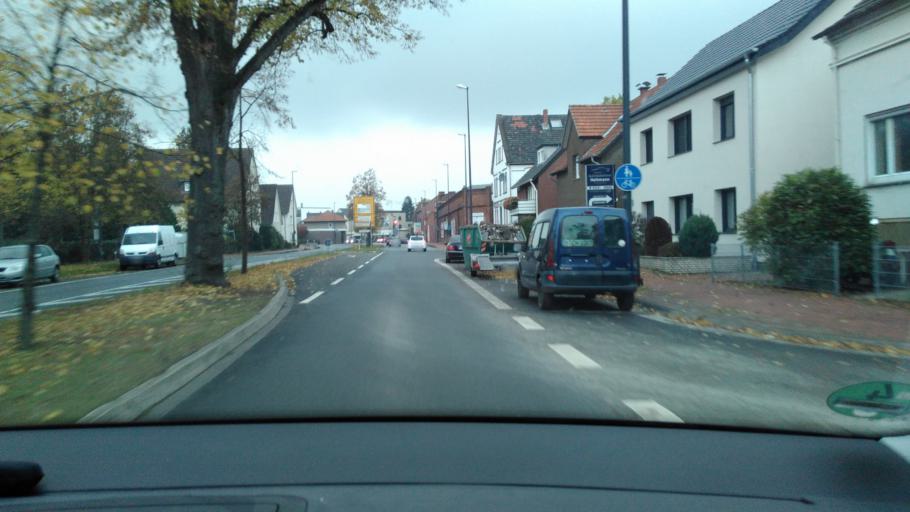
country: DE
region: North Rhine-Westphalia
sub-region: Regierungsbezirk Detmold
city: Guetersloh
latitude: 51.9031
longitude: 8.3952
